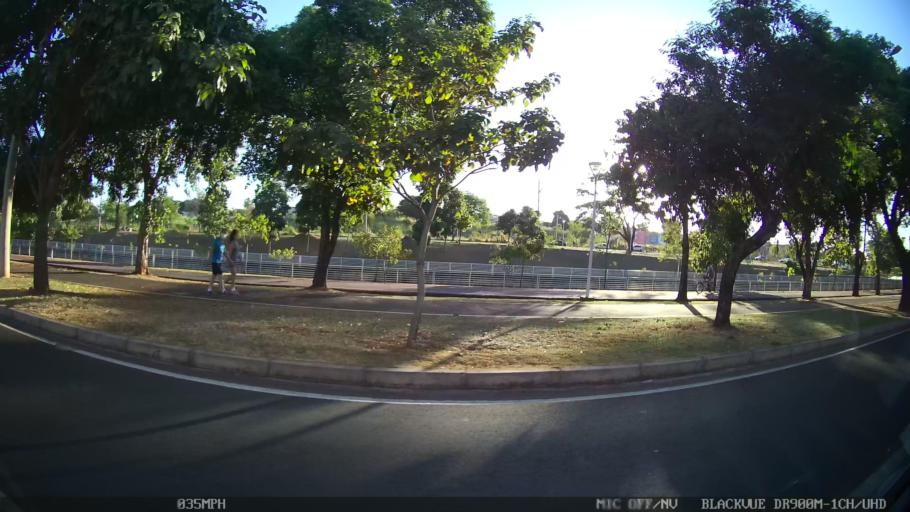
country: BR
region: Sao Paulo
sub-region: Sao Jose Do Rio Preto
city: Sao Jose do Rio Preto
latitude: -20.7937
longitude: -49.3762
